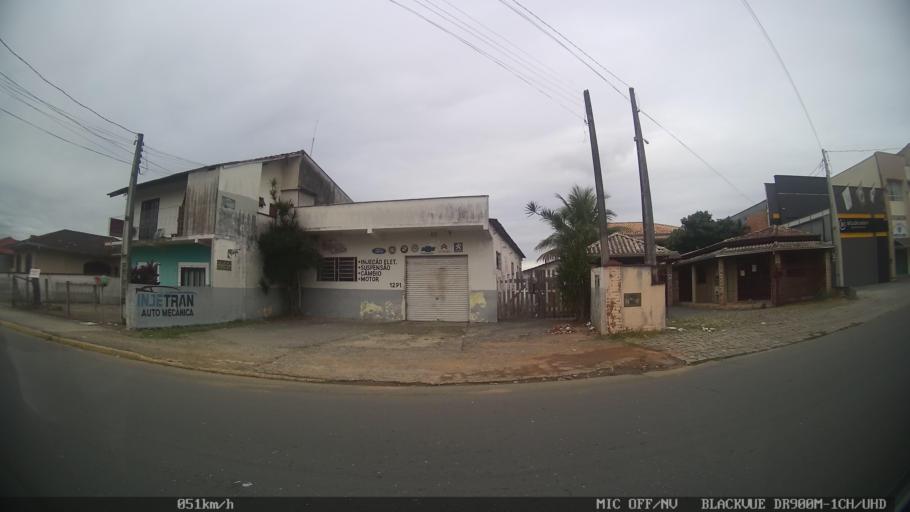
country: BR
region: Santa Catarina
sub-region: Joinville
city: Joinville
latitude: -26.2623
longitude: -48.8180
